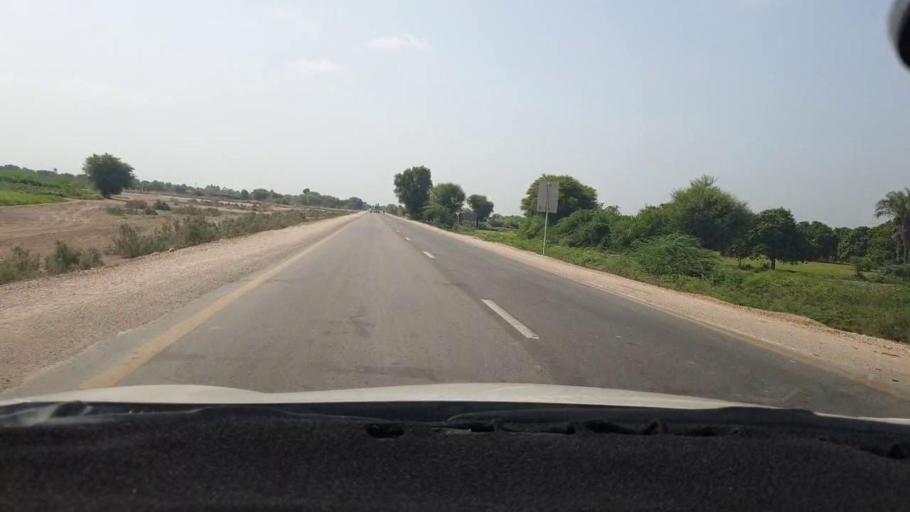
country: PK
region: Sindh
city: Mirpur Khas
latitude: 25.6329
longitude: 69.0927
